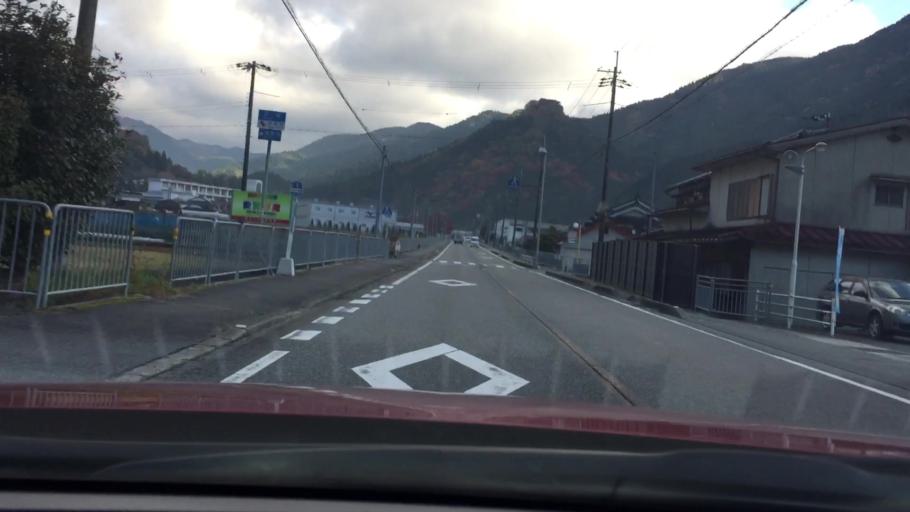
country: JP
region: Hyogo
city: Yamazakicho-nakabirose
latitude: 35.1503
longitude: 134.5411
